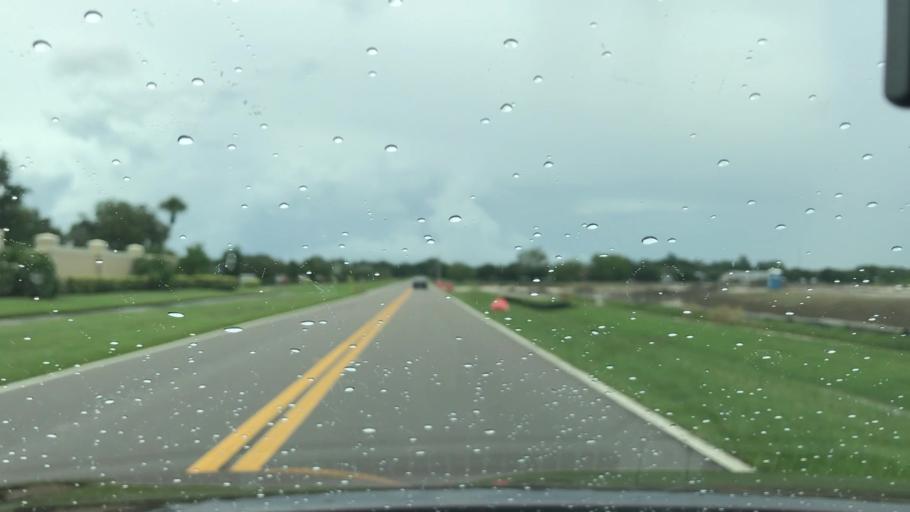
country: US
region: Florida
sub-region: Sarasota County
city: Lake Sarasota
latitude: 27.3134
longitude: -82.3945
